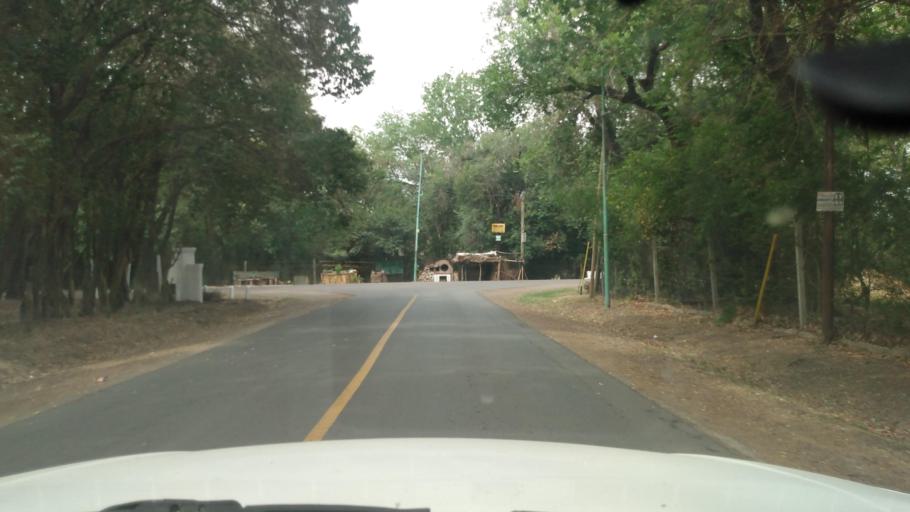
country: AR
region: Buenos Aires
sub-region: Partido de Lujan
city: Lujan
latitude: -34.5531
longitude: -59.1959
